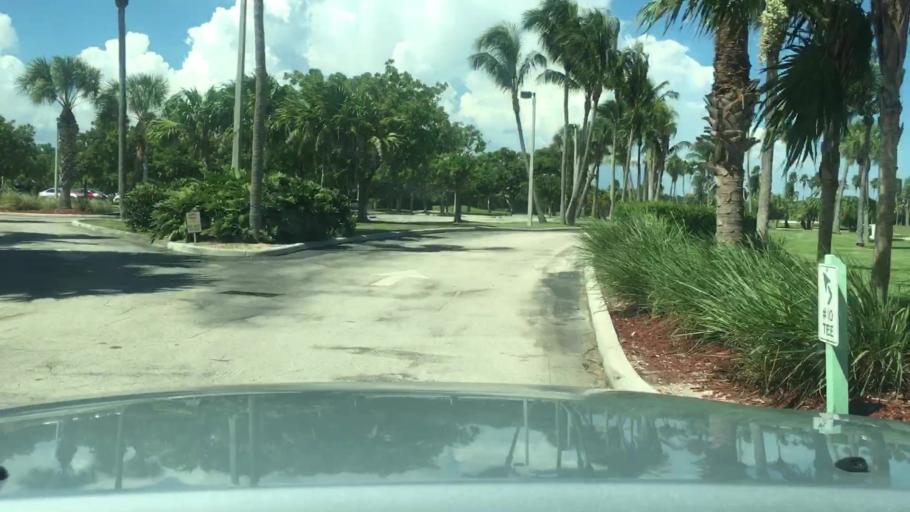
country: US
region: Florida
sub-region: Miami-Dade County
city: Key Biscayne
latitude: 25.7156
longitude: -80.1580
